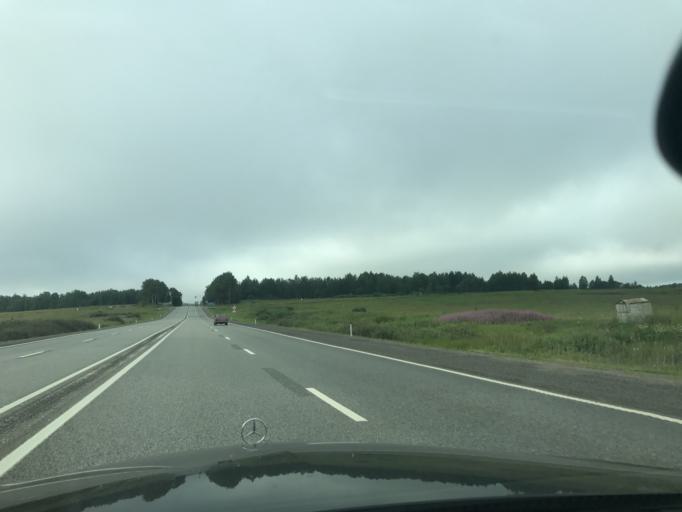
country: RU
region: Smolensk
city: Vyaz'ma
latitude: 55.3352
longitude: 34.5886
